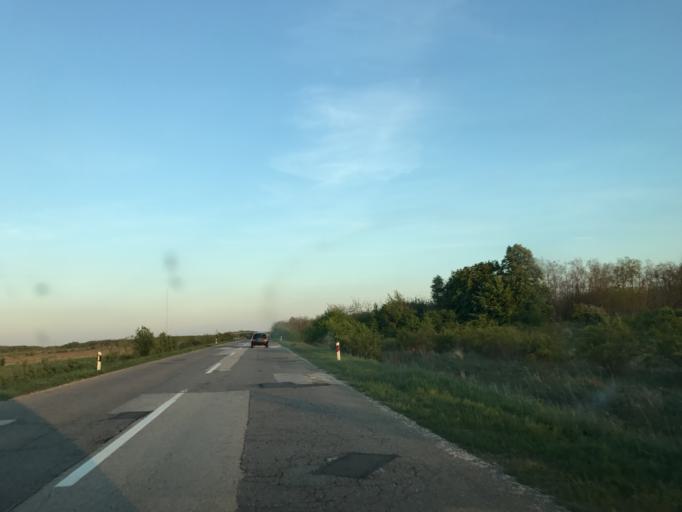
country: RO
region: Mehedinti
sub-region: Comuna Gogosu
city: Ostrovu Mare
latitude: 44.3229
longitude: 22.4878
